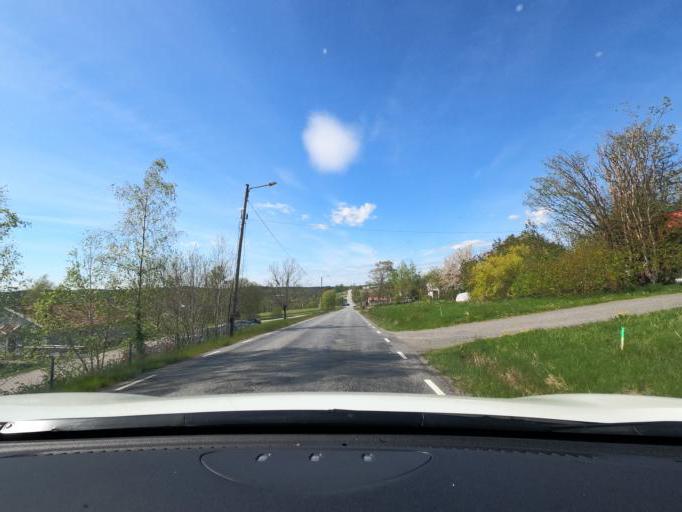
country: SE
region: Vaestra Goetaland
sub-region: Marks Kommun
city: Bua
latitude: 57.5010
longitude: 12.5522
